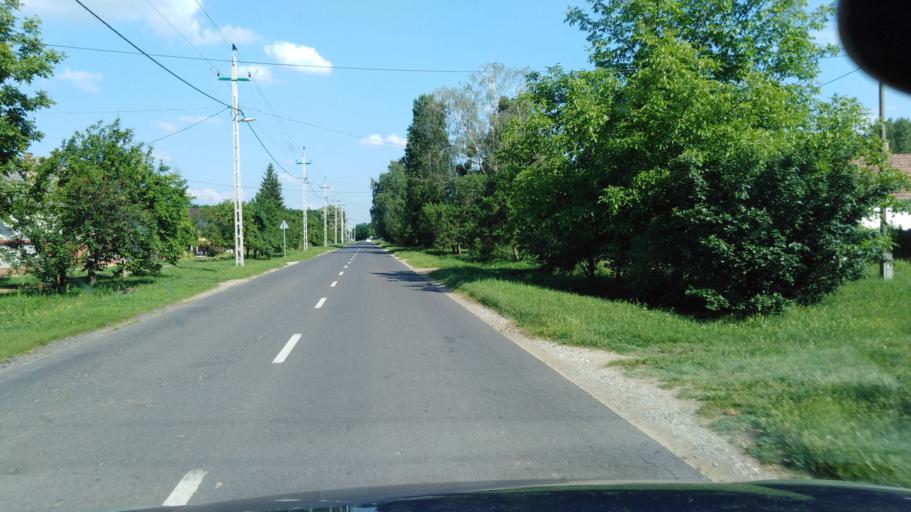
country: HU
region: Szabolcs-Szatmar-Bereg
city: Nyirvasvari
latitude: 47.8136
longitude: 22.1990
